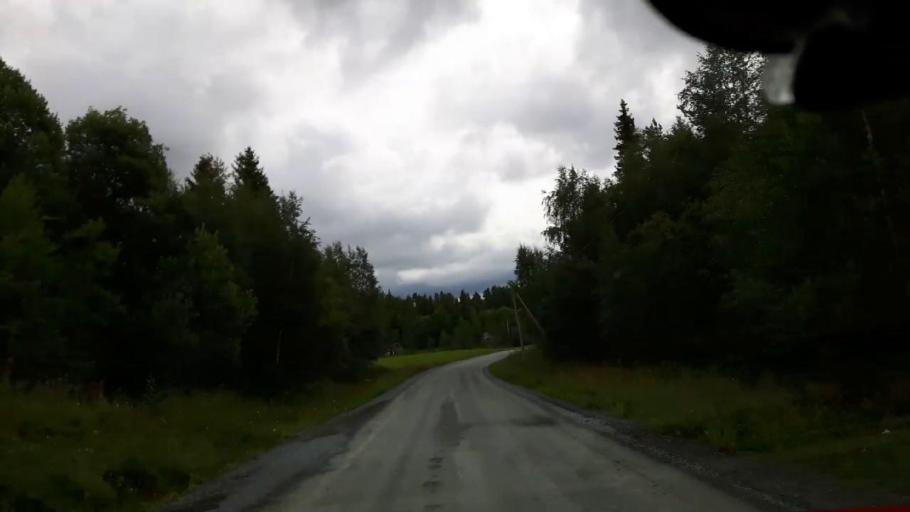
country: SE
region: Jaemtland
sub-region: Krokoms Kommun
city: Krokom
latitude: 63.5733
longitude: 14.2393
